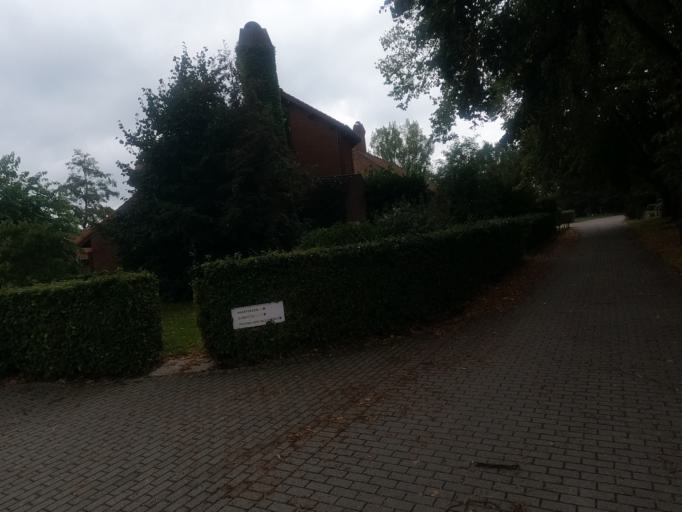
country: BE
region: Flanders
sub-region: Provincie Antwerpen
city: Berlaar
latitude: 51.1379
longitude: 4.6592
